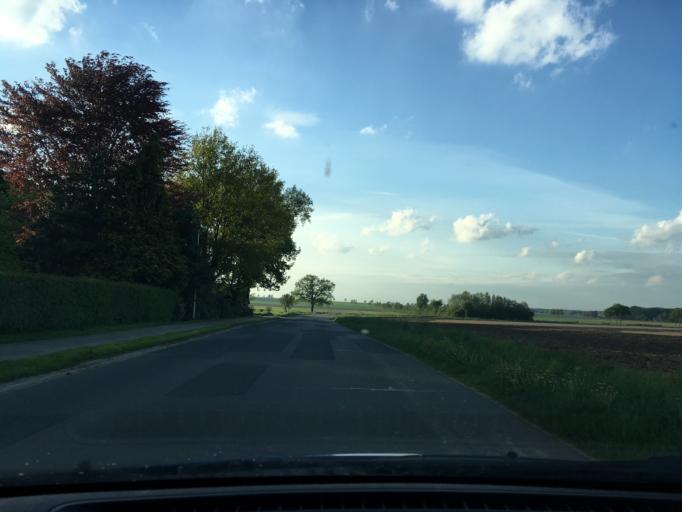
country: DE
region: Lower Saxony
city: Bergen
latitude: 52.8289
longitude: 9.9706
